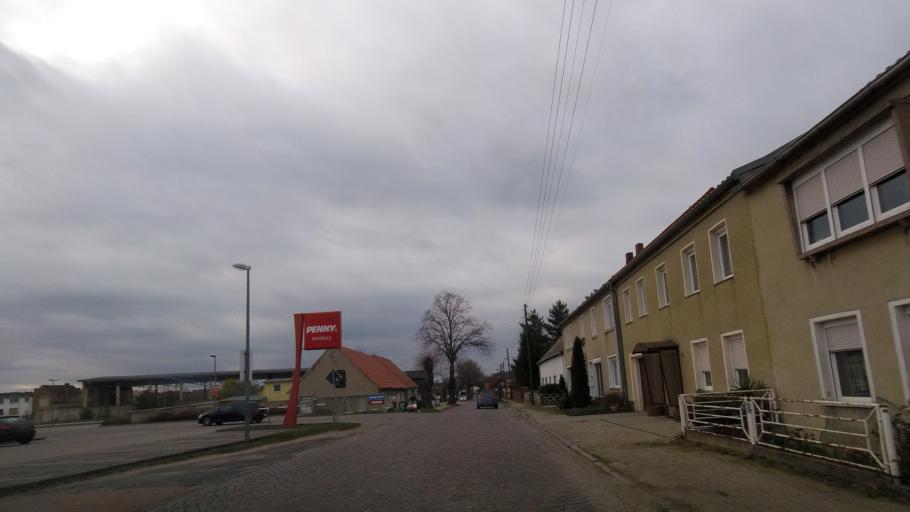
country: DE
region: Saxony-Anhalt
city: Kemberg
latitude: 51.7677
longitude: 12.6338
